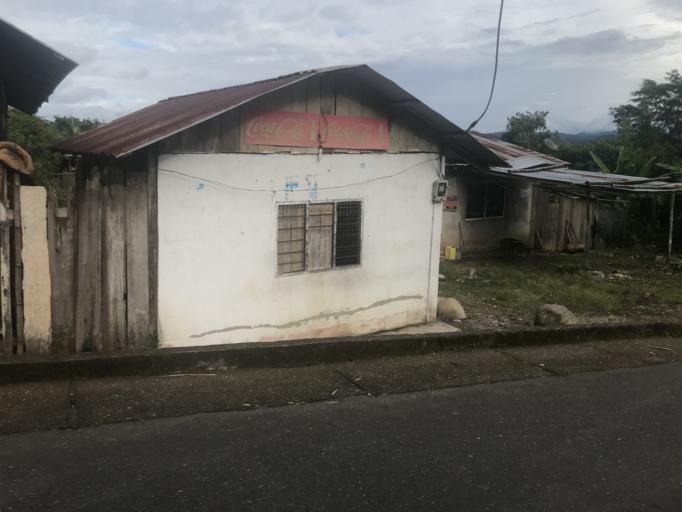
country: EC
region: Napo
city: Tena
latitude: -1.0456
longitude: -77.8094
